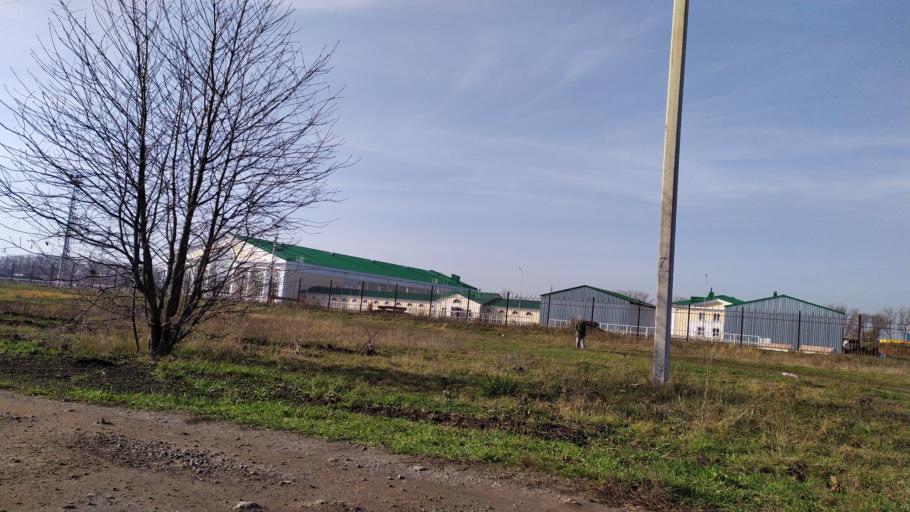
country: RU
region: Kursk
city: Kursk
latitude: 51.6425
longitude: 36.1315
